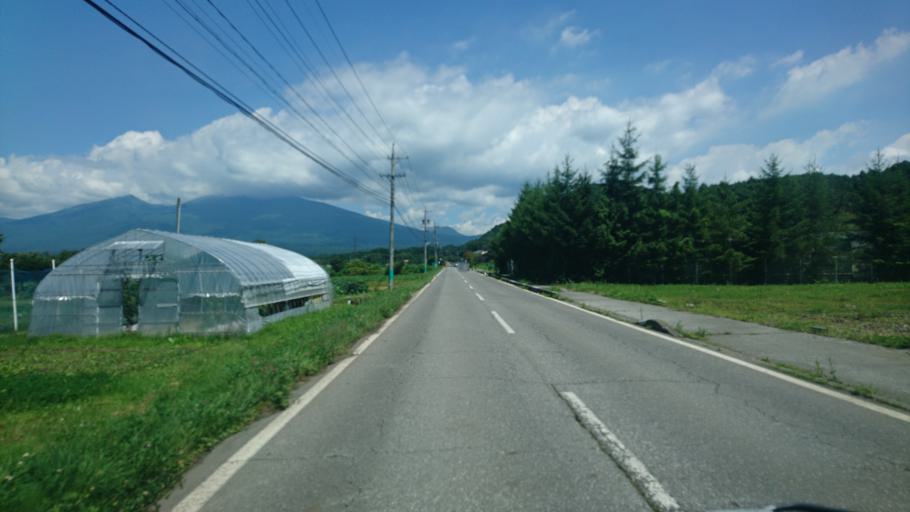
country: JP
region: Nagano
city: Saku
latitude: 36.3160
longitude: 138.5919
